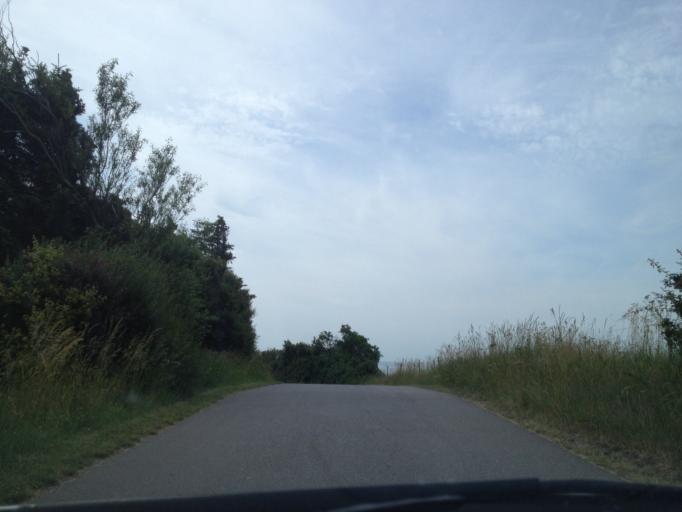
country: DK
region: Central Jutland
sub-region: Samso Kommune
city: Tranebjerg
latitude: 55.9697
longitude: 10.5273
